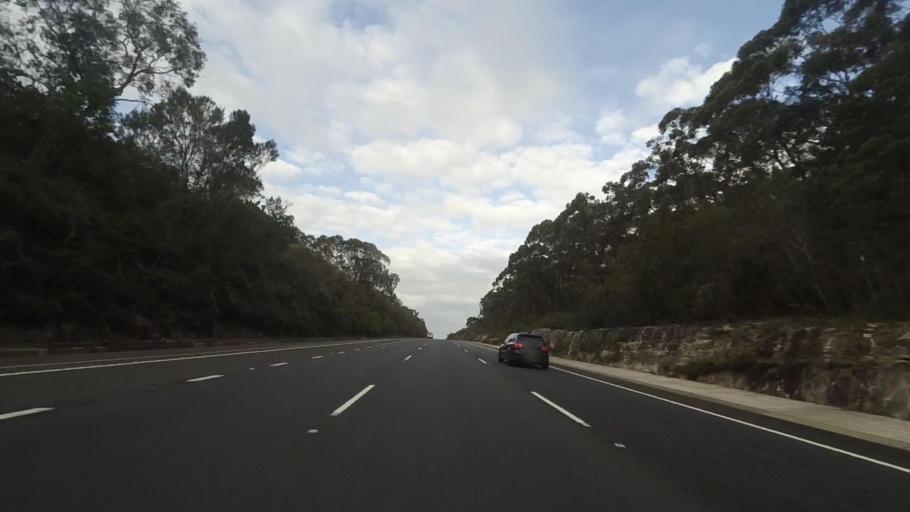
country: AU
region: New South Wales
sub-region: Wollongong
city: Bulli
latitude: -34.3004
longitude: 150.9096
